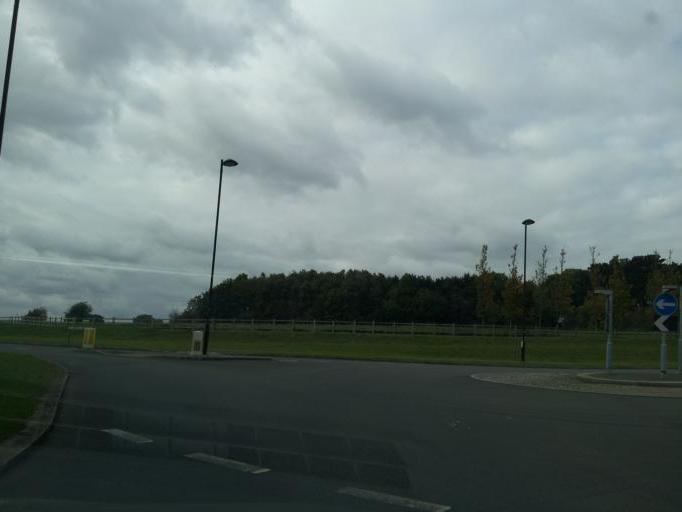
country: GB
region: England
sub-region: Northamptonshire
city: Blisworth
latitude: 52.2372
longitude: -0.9485
